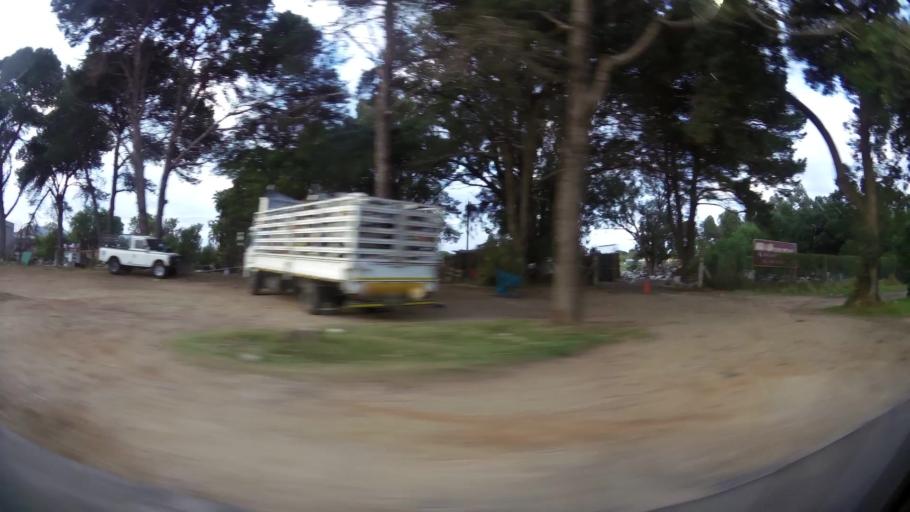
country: ZA
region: Eastern Cape
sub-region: Nelson Mandela Bay Metropolitan Municipality
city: Port Elizabeth
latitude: -33.9829
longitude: 25.5909
